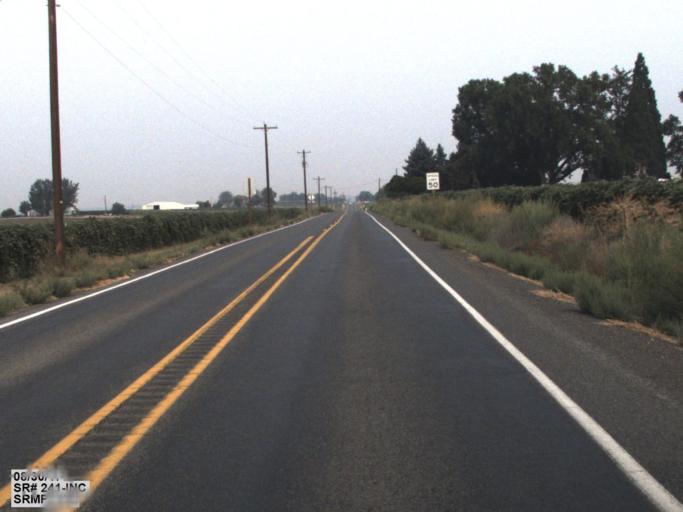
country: US
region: Washington
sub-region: Yakima County
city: Sunnyside
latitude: 46.3325
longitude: -119.9790
